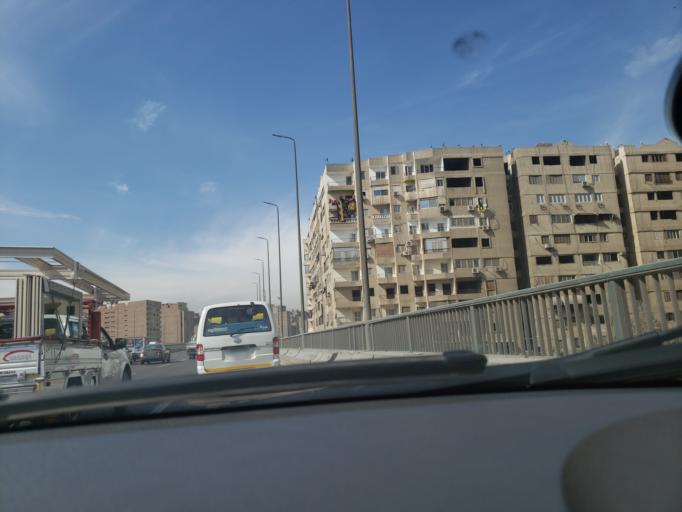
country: EG
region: Al Jizah
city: Al Jizah
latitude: 29.9788
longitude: 31.1612
